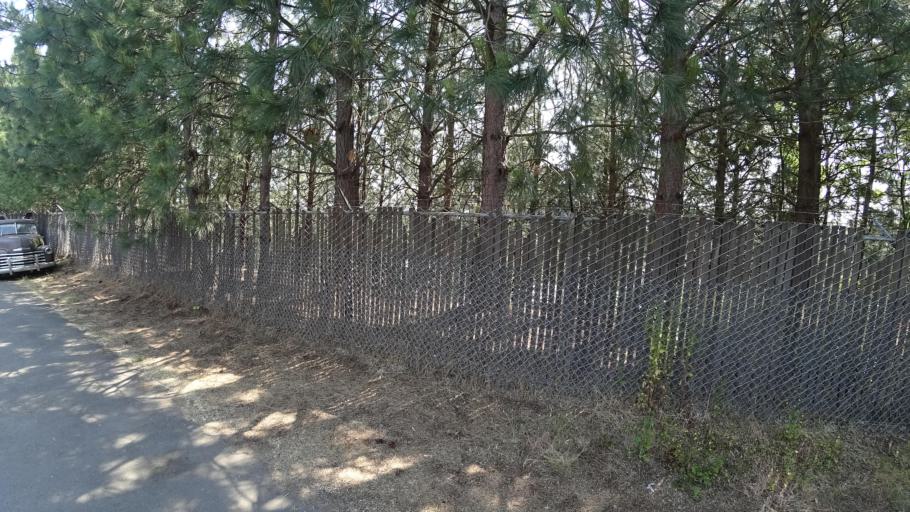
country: US
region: Oregon
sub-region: Clackamas County
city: Oatfield
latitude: 45.4490
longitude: -122.5896
